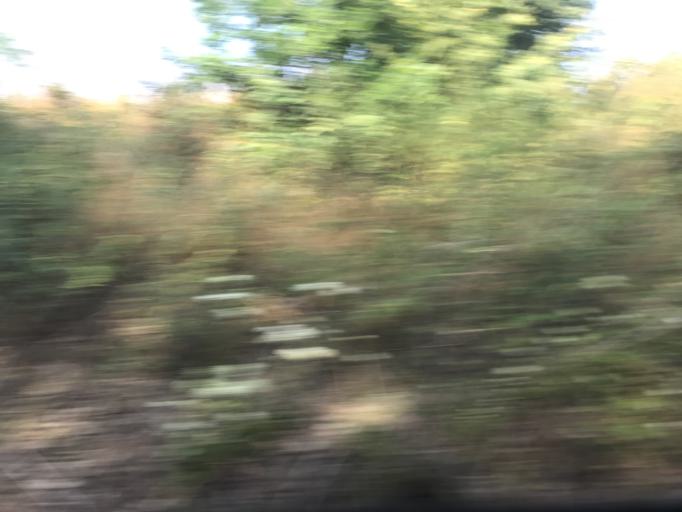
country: CZ
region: Central Bohemia
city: Votice
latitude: 49.5707
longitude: 14.6104
